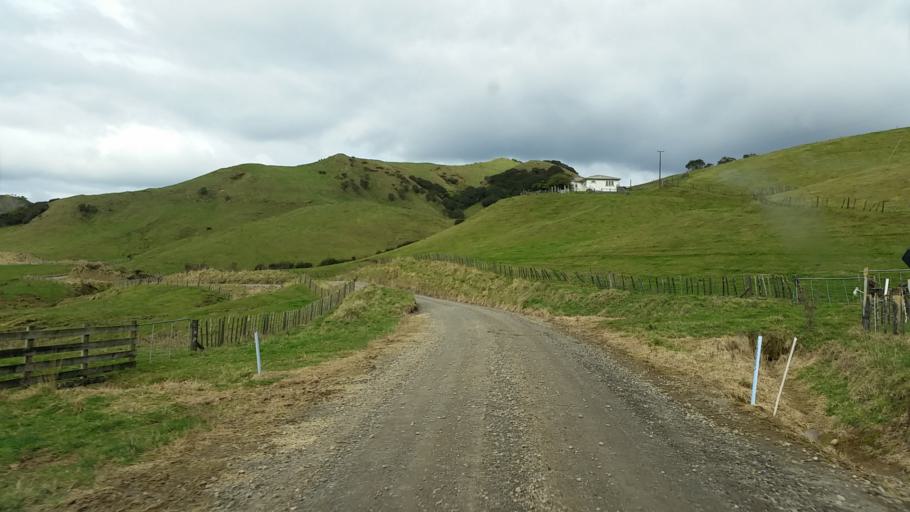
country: NZ
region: Taranaki
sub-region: South Taranaki District
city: Eltham
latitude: -39.1678
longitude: 174.6027
